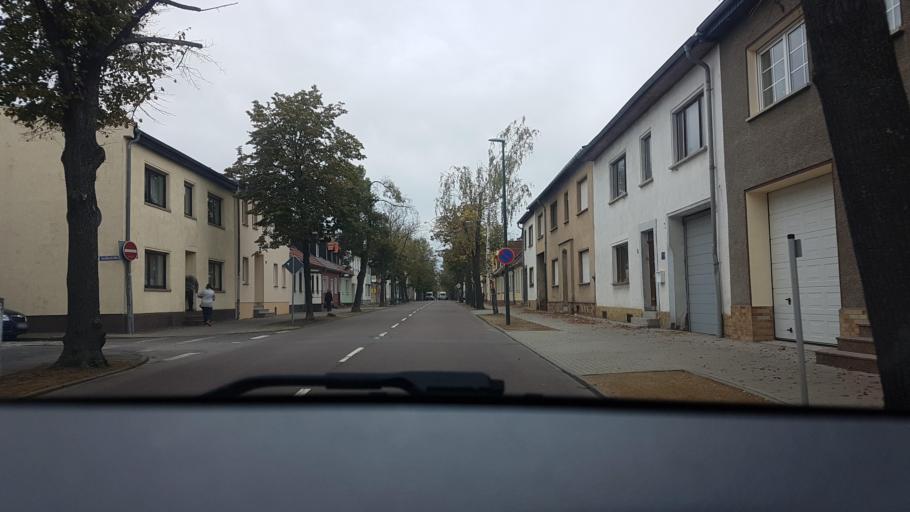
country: DE
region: Saxony-Anhalt
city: Bernburg
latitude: 51.7905
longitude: 11.7385
